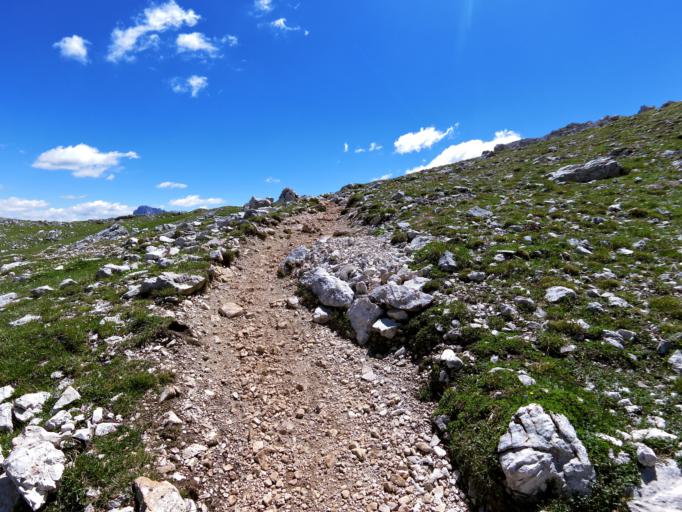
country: IT
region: Trentino-Alto Adige
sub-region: Bolzano
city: Siusi
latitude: 46.5039
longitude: 11.5956
